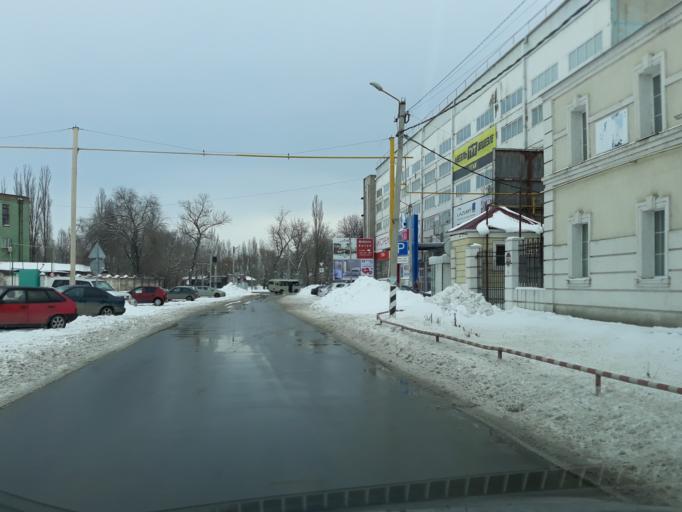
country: RU
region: Rostov
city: Taganrog
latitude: 47.2153
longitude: 38.9358
